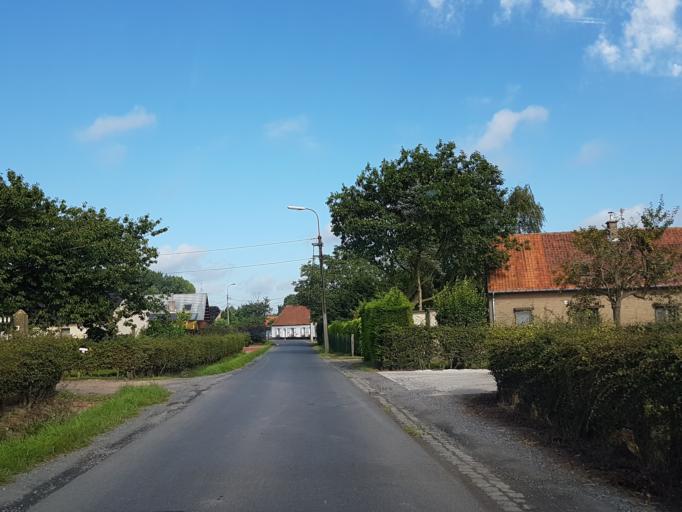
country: BE
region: Flanders
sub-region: Provincie Oost-Vlaanderen
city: Nevele
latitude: 51.0637
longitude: 3.5610
